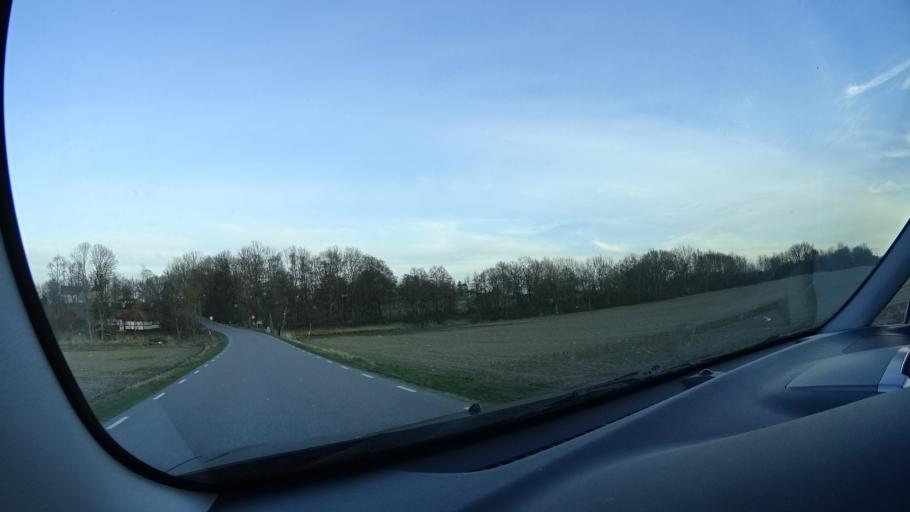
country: SE
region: Skane
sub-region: Eslovs Kommun
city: Stehag
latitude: 55.8980
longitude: 13.4115
